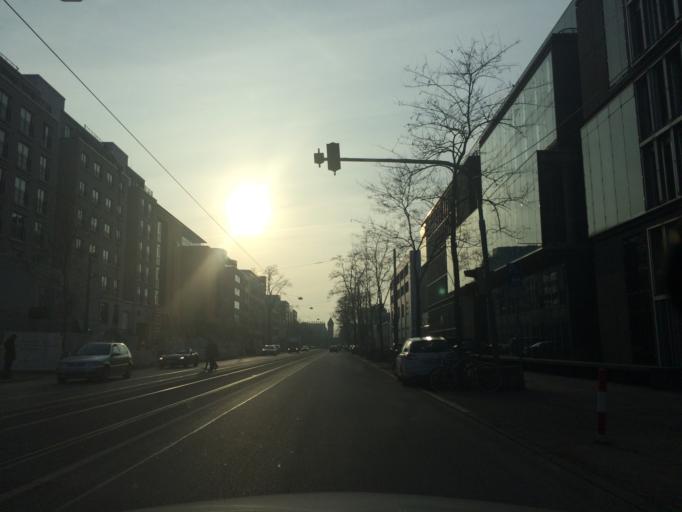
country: DE
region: Hesse
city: Niederrad
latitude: 50.1054
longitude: 8.6502
